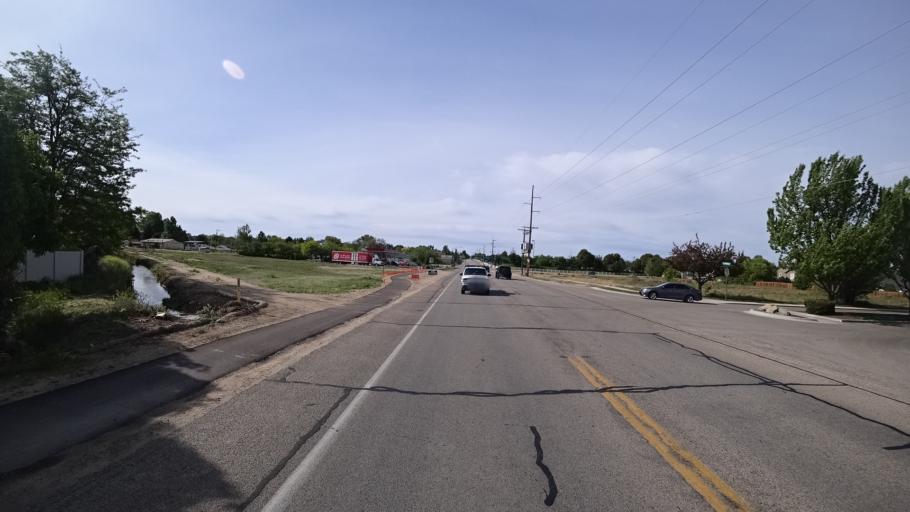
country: US
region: Idaho
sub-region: Ada County
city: Meridian
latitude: 43.5483
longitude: -116.3344
